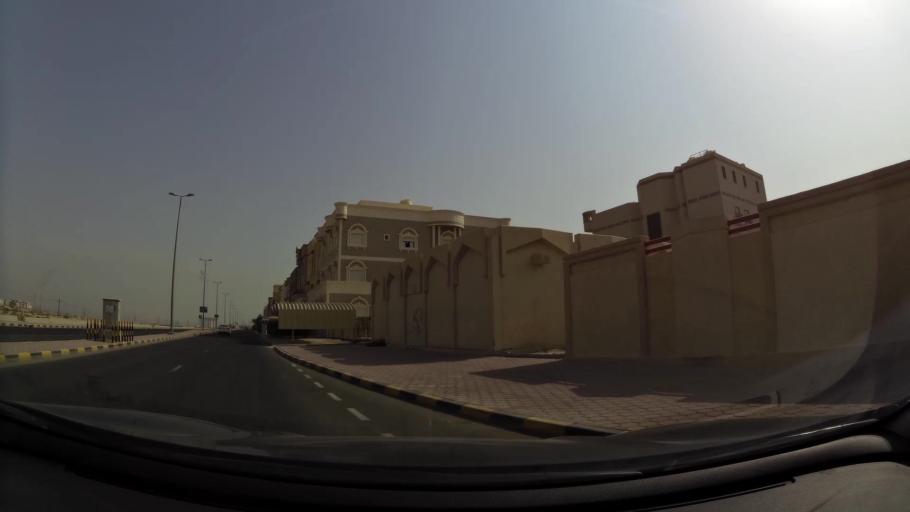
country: KW
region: Muhafazat al Jahra'
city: Al Jahra'
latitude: 29.3310
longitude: 47.7707
